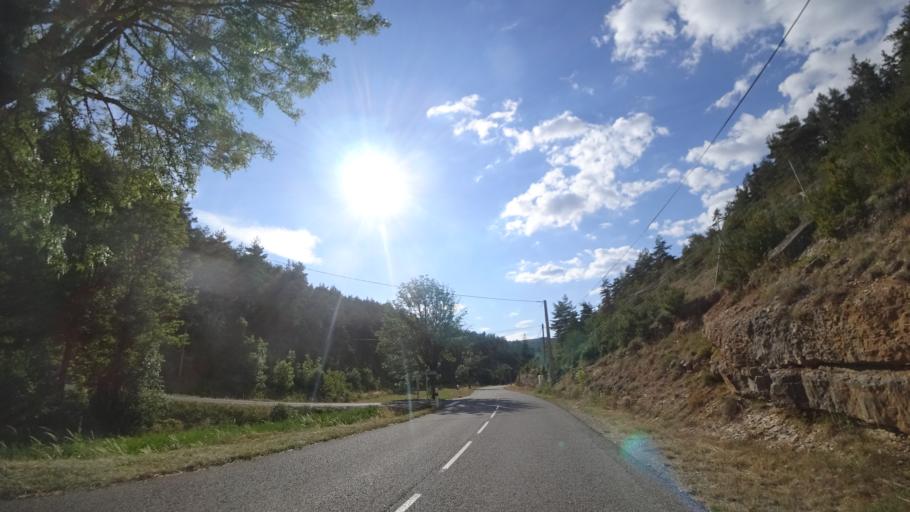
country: FR
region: Languedoc-Roussillon
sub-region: Departement de la Lozere
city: La Canourgue
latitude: 44.4078
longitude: 3.2792
